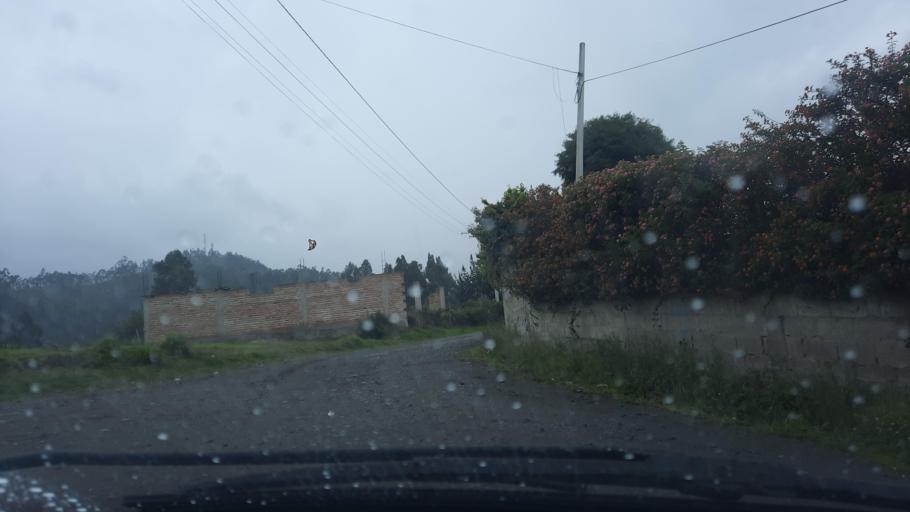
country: EC
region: Chimborazo
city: Riobamba
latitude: -1.6900
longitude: -78.6568
